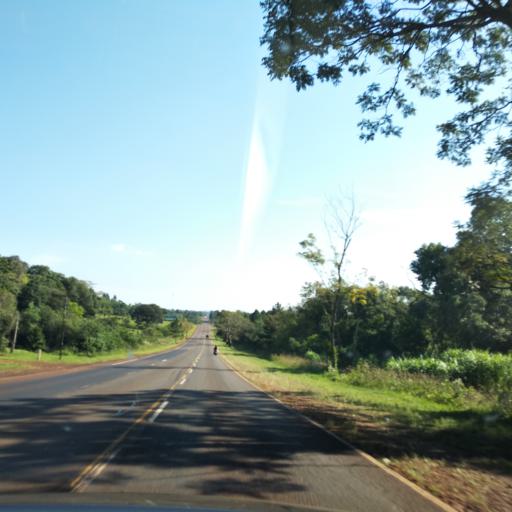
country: AR
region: Misiones
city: Jardin America
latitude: -27.0757
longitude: -55.2774
